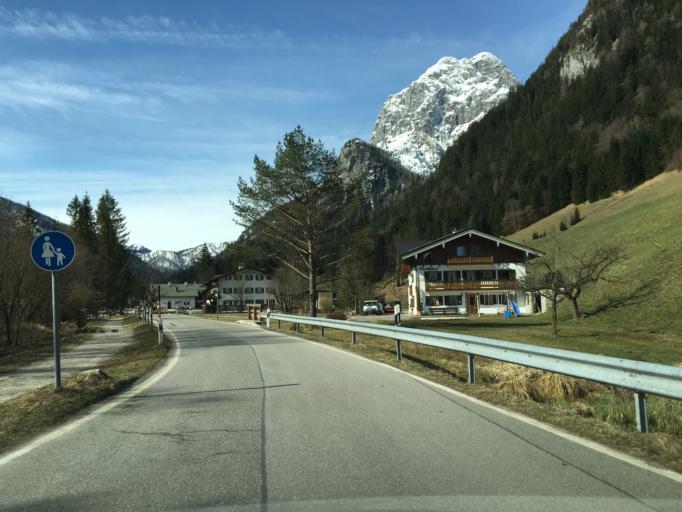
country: DE
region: Bavaria
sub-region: Upper Bavaria
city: Ramsau
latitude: 47.6016
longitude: 12.8465
